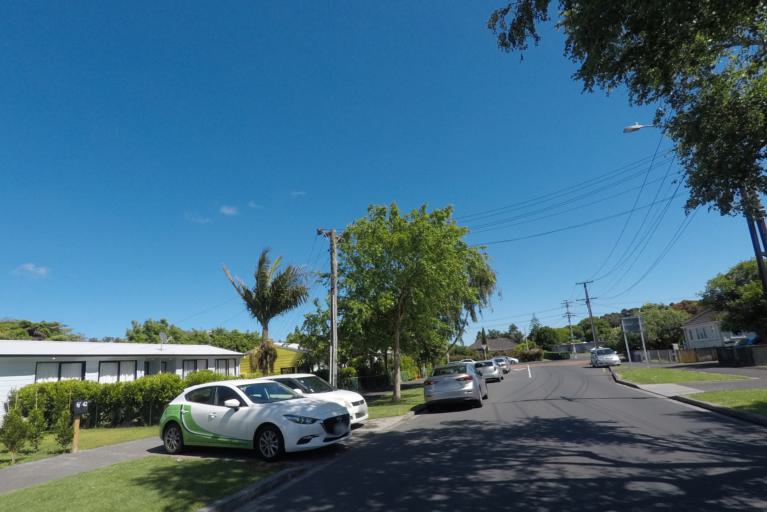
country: NZ
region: Auckland
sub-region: Auckland
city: Rosebank
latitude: -36.8929
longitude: 174.6854
